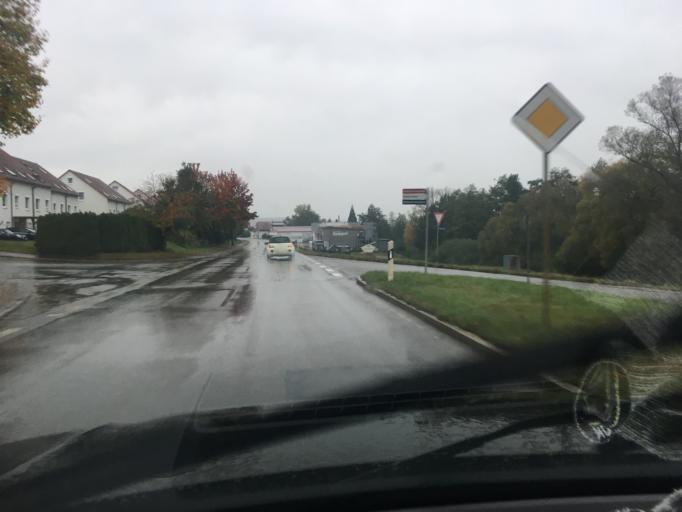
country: DE
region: Baden-Wuerttemberg
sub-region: Tuebingen Region
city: Nehren
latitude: 48.4365
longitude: 9.0742
